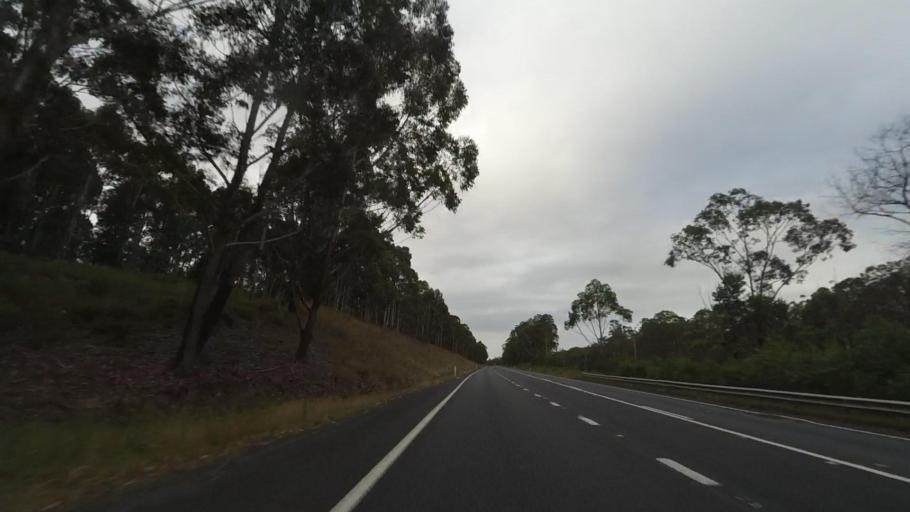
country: AU
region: New South Wales
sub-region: Shoalhaven Shire
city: Milton
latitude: -35.1277
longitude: 150.4717
